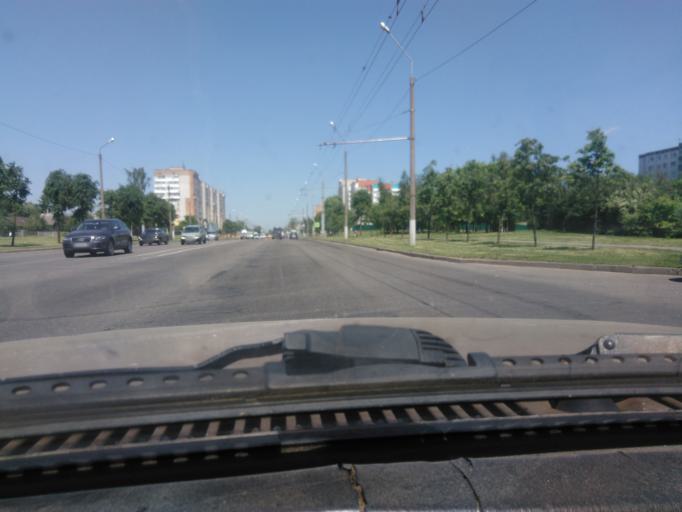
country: BY
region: Mogilev
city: Mahilyow
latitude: 53.9305
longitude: 30.3516
